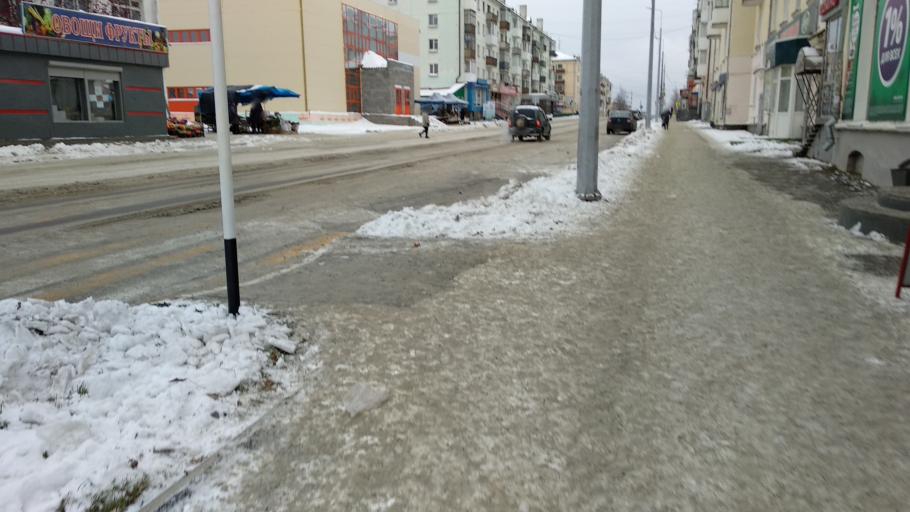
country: RU
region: Sverdlovsk
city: Krasnotur'insk
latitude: 59.7633
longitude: 60.2031
